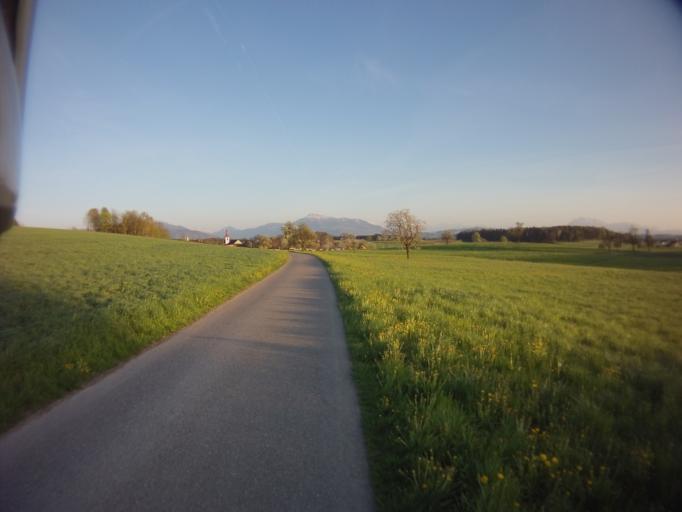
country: CH
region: Zurich
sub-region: Bezirk Affoltern
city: Knonau
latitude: 47.2175
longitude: 8.4493
